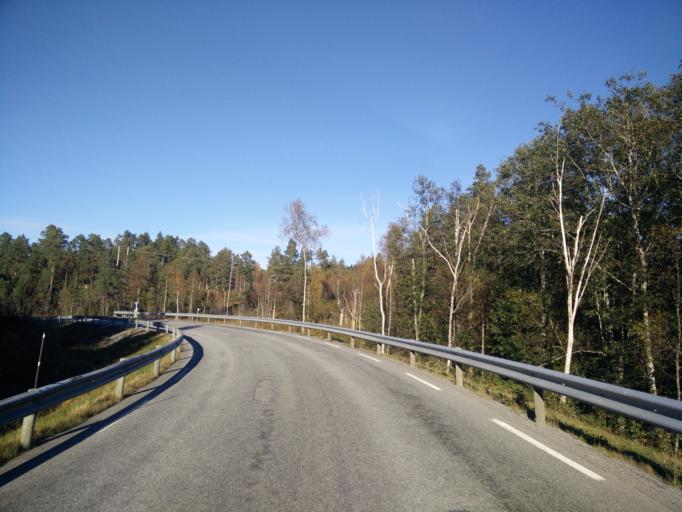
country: NO
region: More og Romsdal
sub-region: Halsa
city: Liaboen
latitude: 63.1046
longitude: 8.3386
